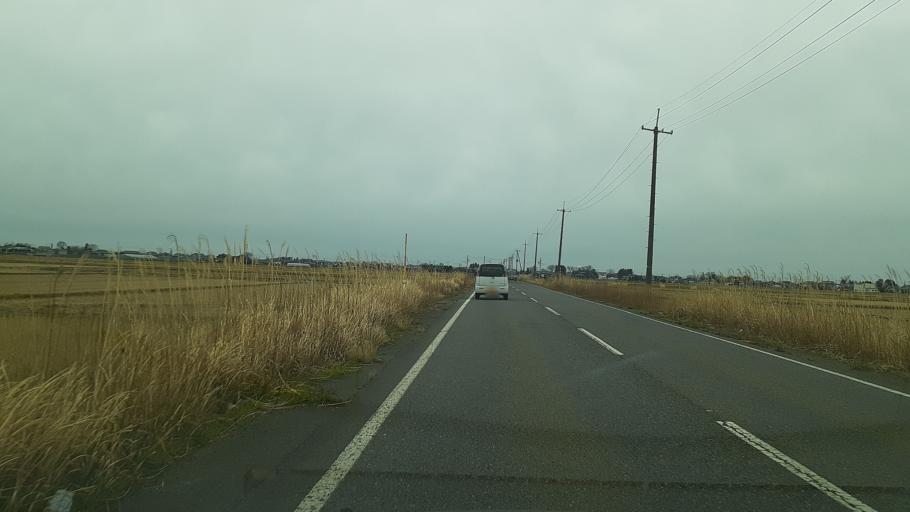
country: JP
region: Niigata
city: Niitsu-honcho
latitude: 37.8281
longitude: 139.0835
